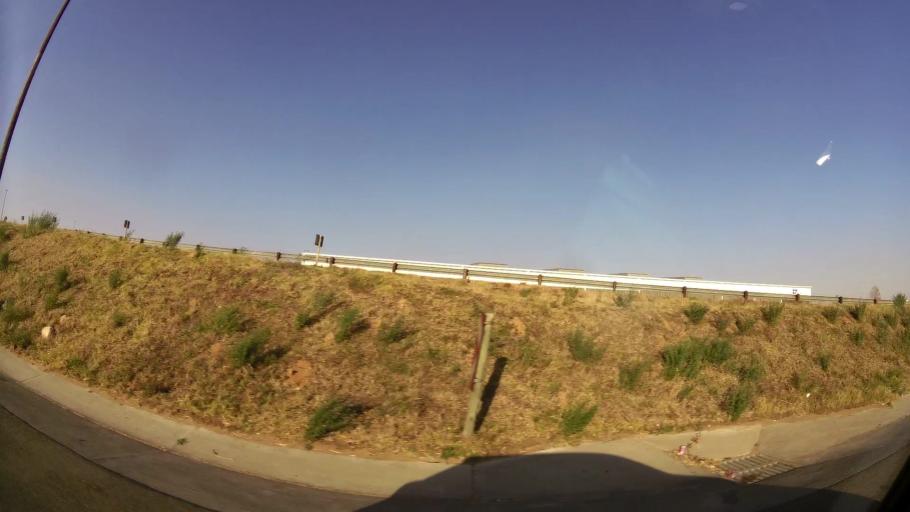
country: ZA
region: Gauteng
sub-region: Ekurhuleni Metropolitan Municipality
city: Germiston
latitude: -26.2431
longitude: 28.1254
